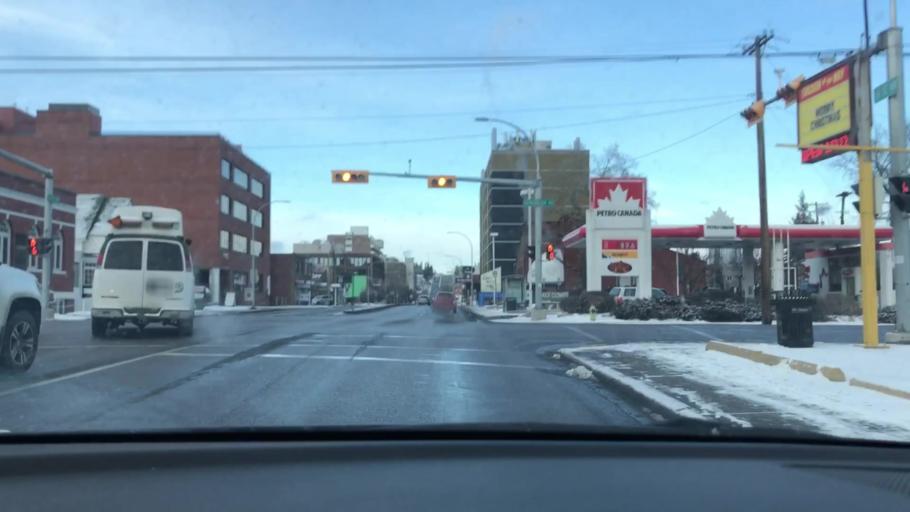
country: CA
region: Alberta
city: Calgary
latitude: 51.0523
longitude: -114.0946
